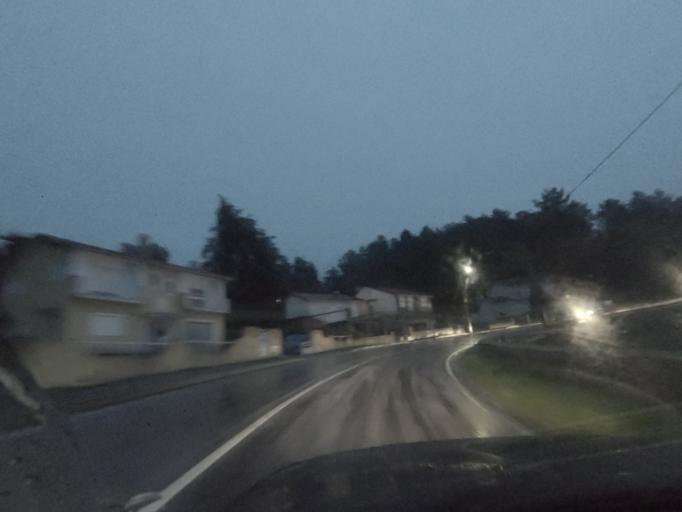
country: PT
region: Vila Real
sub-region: Vila Real
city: Vila Real
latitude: 41.2905
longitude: -7.7038
